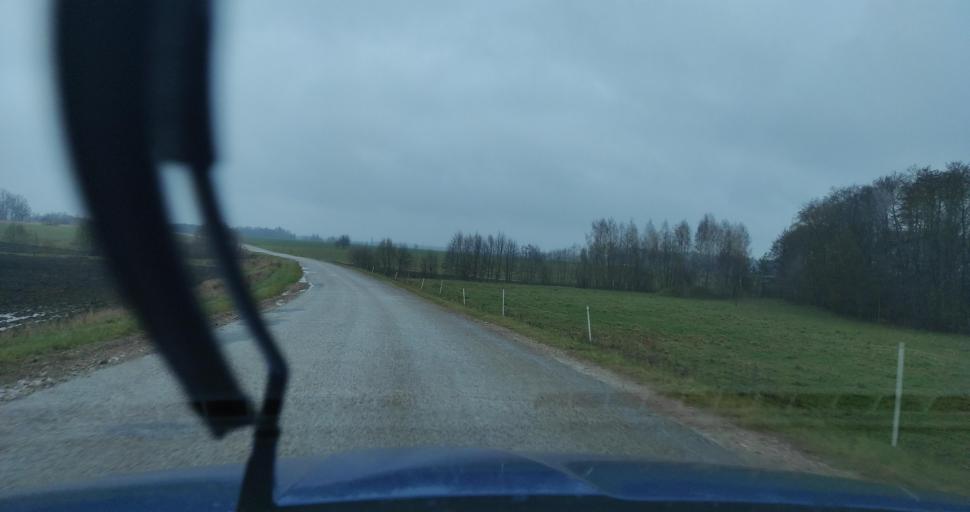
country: LV
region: Alsunga
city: Alsunga
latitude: 56.8985
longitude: 21.6152
